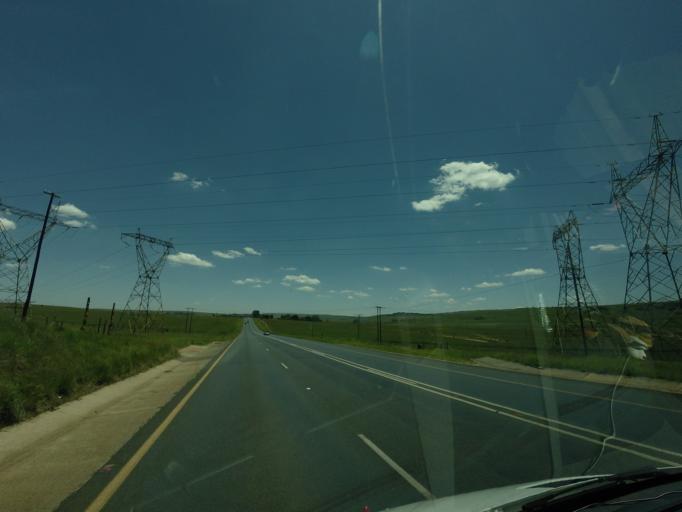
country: ZA
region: Mpumalanga
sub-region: Nkangala District Municipality
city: Belfast
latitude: -25.6797
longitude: 30.2257
